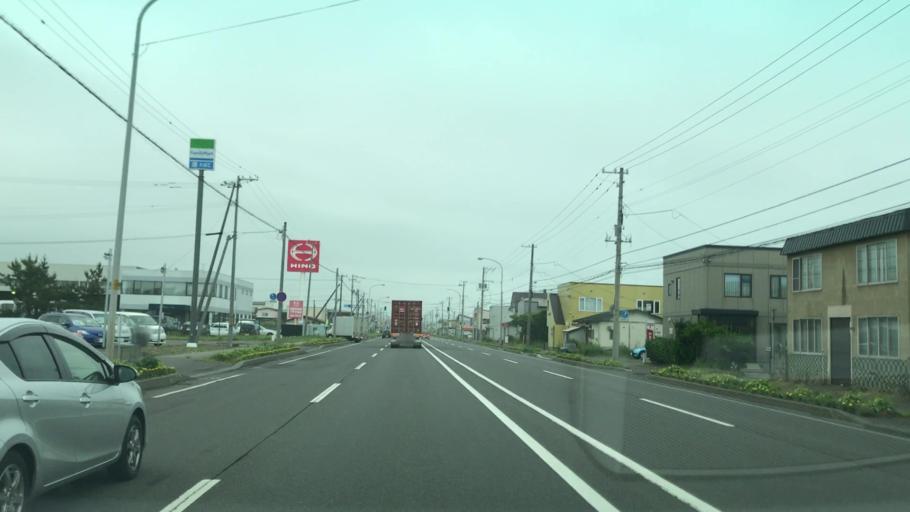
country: JP
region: Hokkaido
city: Muroran
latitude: 42.3717
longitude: 141.0646
